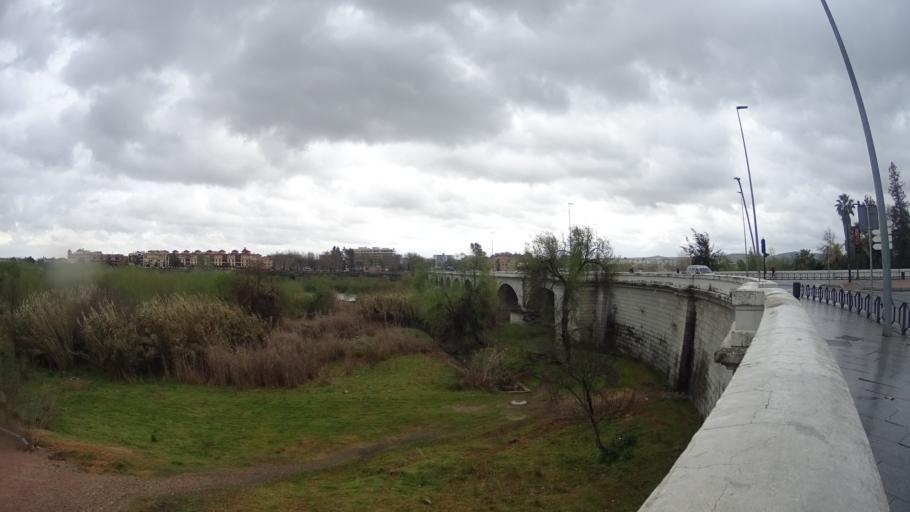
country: ES
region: Andalusia
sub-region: Province of Cordoba
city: Cordoba
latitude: 37.8731
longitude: -4.7838
